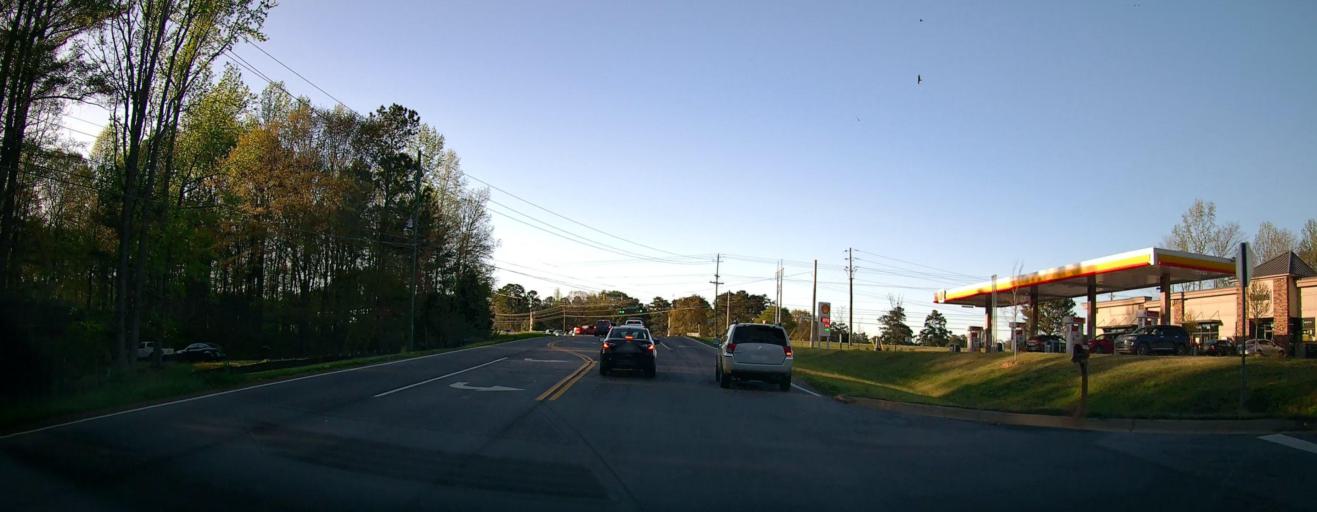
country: US
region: Georgia
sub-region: Newton County
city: Porterdale
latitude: 33.5832
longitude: -83.9081
